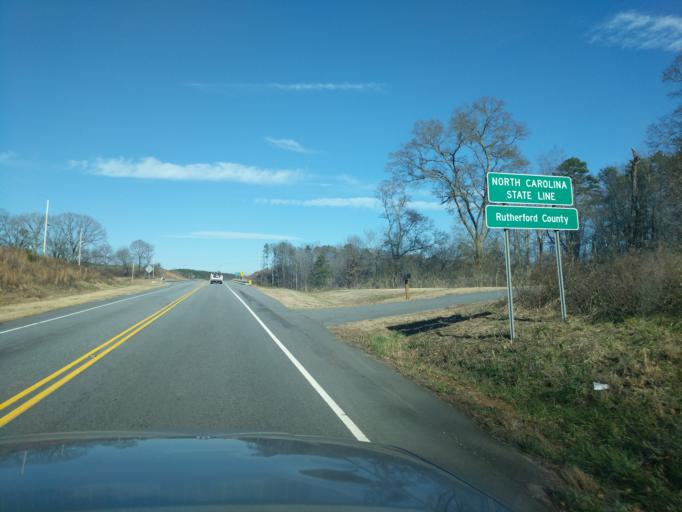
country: US
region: South Carolina
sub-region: Spartanburg County
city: Mayo
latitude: 35.1827
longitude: -81.8440
